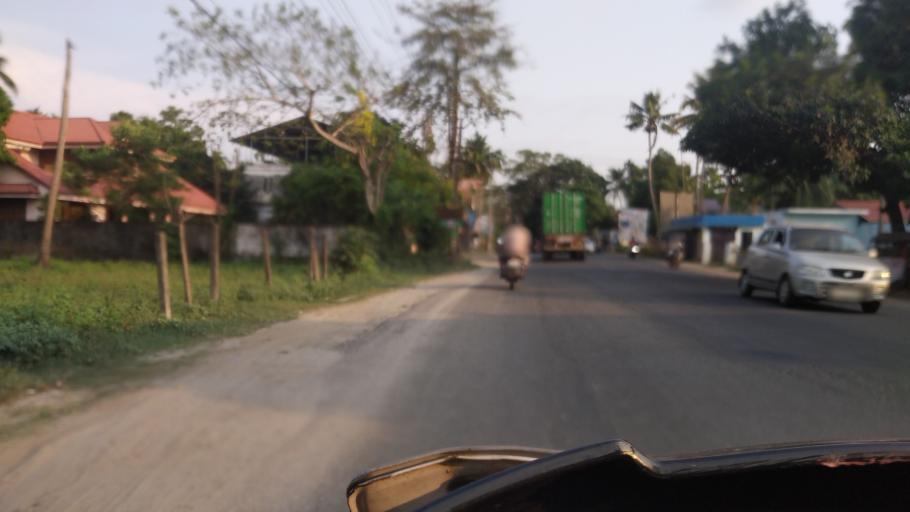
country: IN
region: Kerala
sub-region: Thrissur District
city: Irinjalakuda
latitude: 10.3365
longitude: 76.1386
